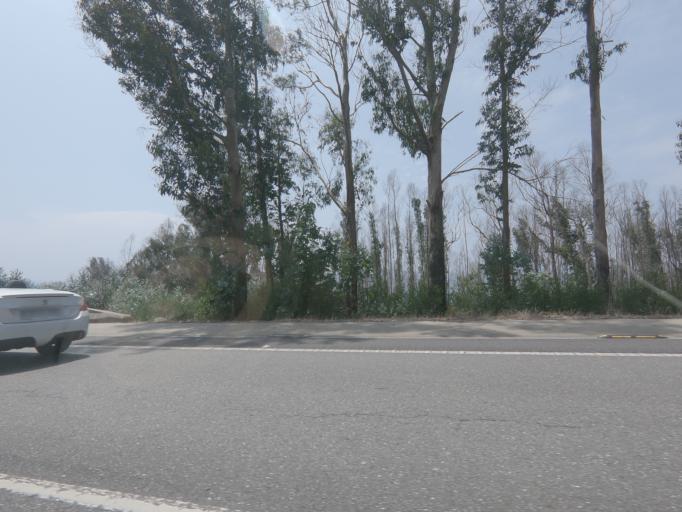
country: ES
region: Galicia
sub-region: Provincia de Pontevedra
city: A Guarda
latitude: 41.9209
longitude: -8.8802
